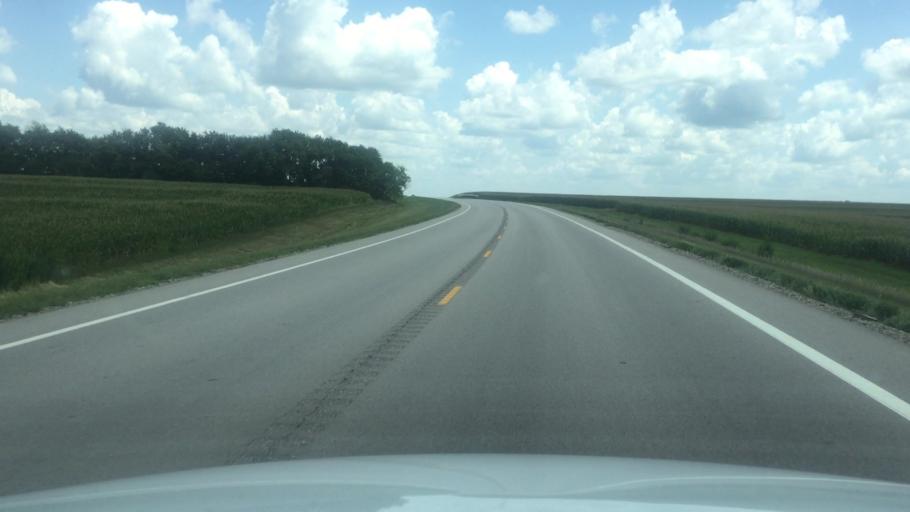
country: US
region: Kansas
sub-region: Brown County
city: Horton
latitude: 39.6605
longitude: -95.4074
